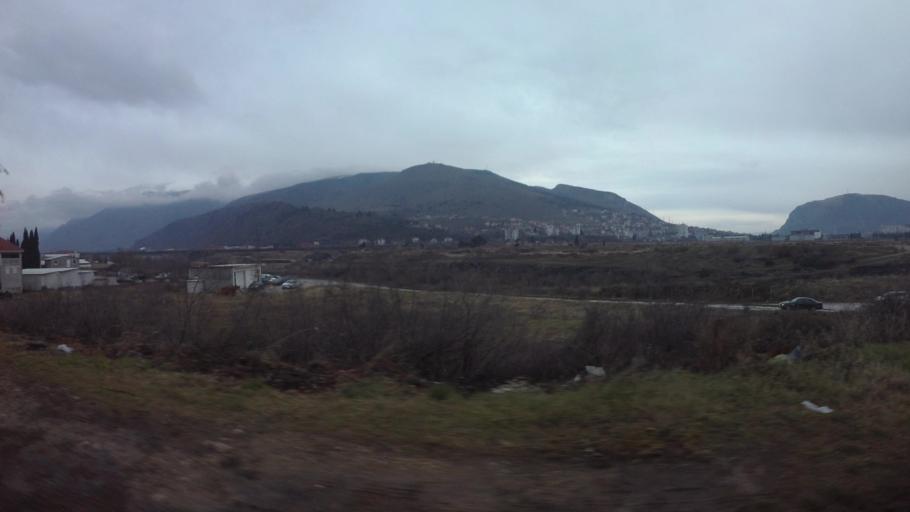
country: BA
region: Federation of Bosnia and Herzegovina
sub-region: Hercegovacko-Bosanski Kanton
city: Mostar
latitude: 43.3656
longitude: 17.8094
